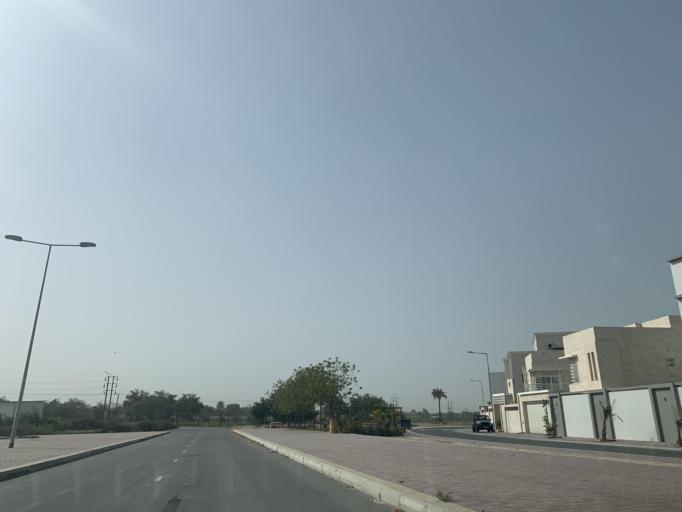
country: BH
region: Northern
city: Madinat `Isa
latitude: 26.1627
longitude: 50.5366
